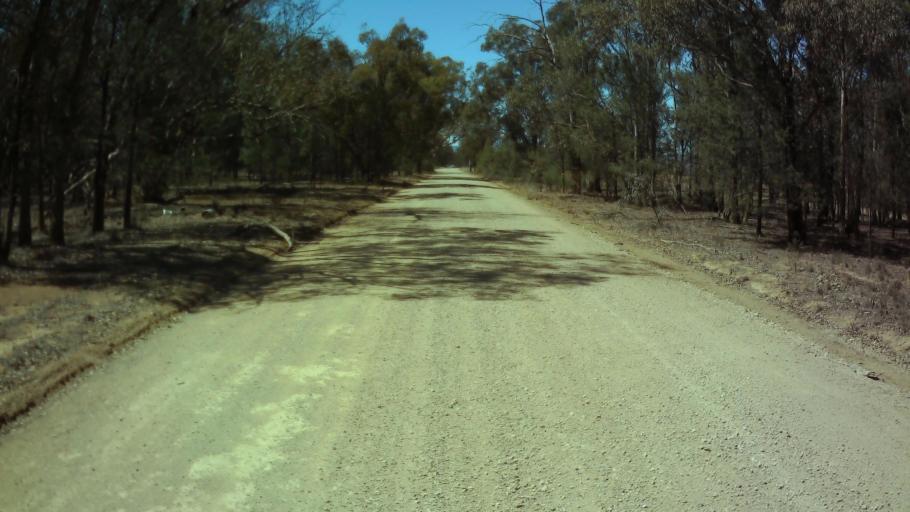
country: AU
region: New South Wales
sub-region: Weddin
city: Grenfell
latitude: -33.8626
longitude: 148.0875
